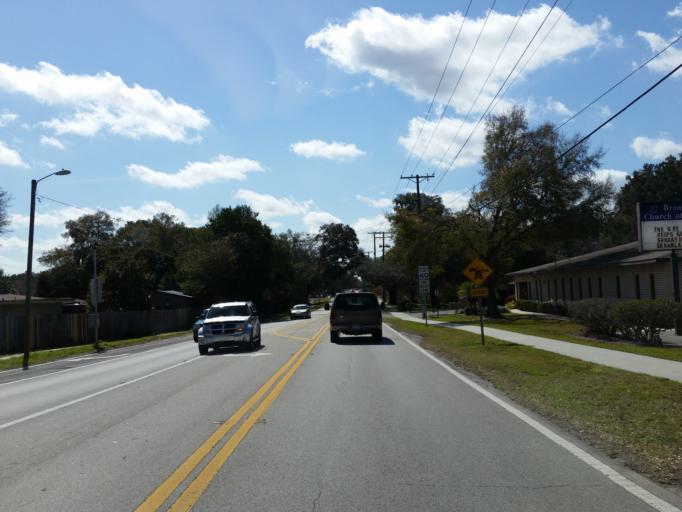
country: US
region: Florida
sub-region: Hillsborough County
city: Brandon
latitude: 27.9449
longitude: -82.2776
